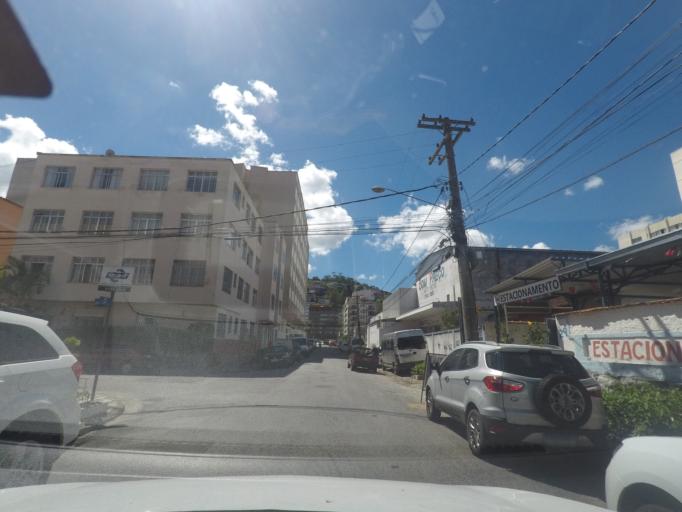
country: BR
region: Rio de Janeiro
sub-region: Teresopolis
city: Teresopolis
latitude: -22.4209
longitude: -42.9744
